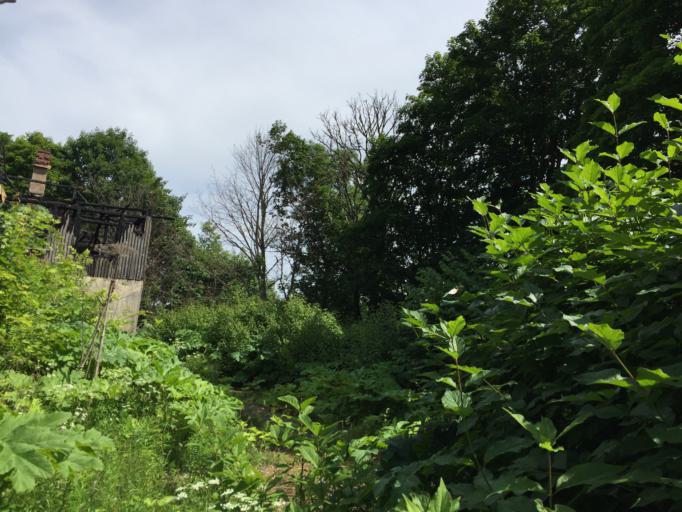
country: LV
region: Pargaujas
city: Stalbe
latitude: 57.3534
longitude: 24.9499
